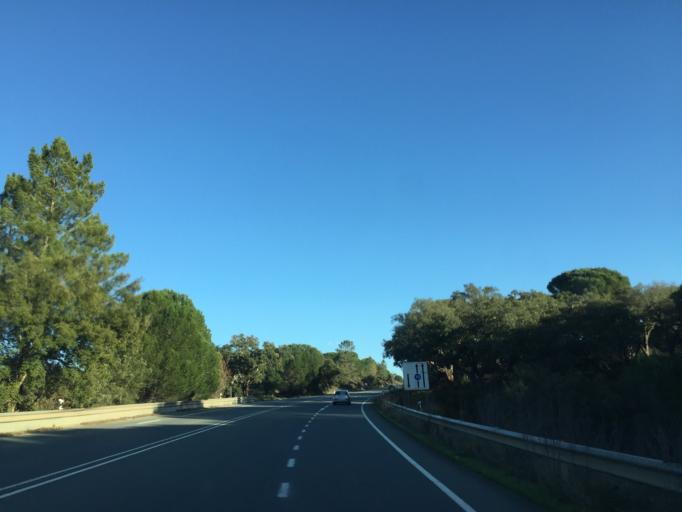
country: PT
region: Setubal
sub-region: Grandola
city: Grandola
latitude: 38.1220
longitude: -8.4307
